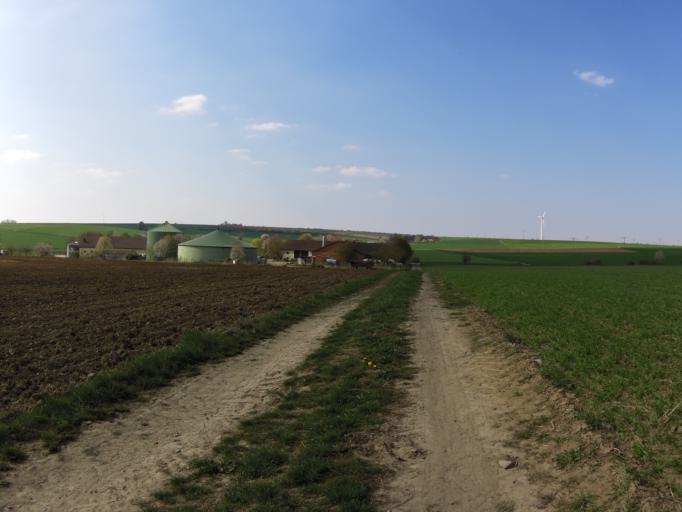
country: DE
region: Bavaria
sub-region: Regierungsbezirk Unterfranken
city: Theilheim
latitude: 49.7605
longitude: 10.0408
